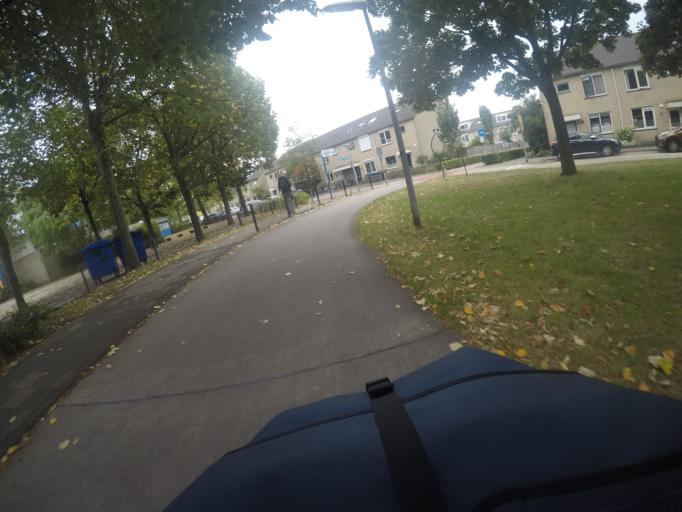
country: NL
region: Flevoland
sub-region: Gemeente Almere
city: Almere Stad
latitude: 52.3647
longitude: 5.1946
